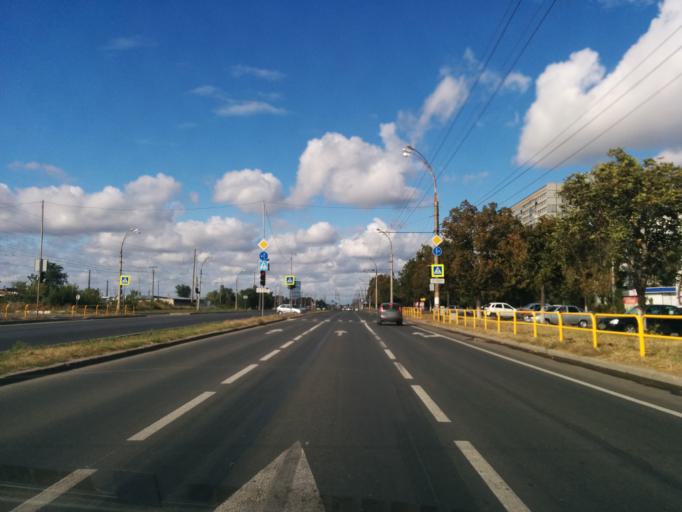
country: RU
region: Samara
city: Tol'yatti
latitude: 53.5362
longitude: 49.2632
